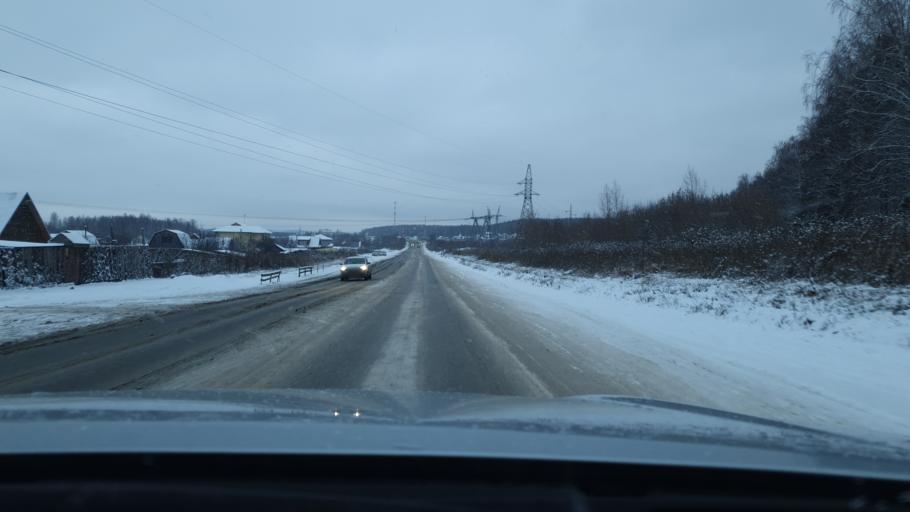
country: RU
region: Sverdlovsk
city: Istok
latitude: 56.7766
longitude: 60.7392
